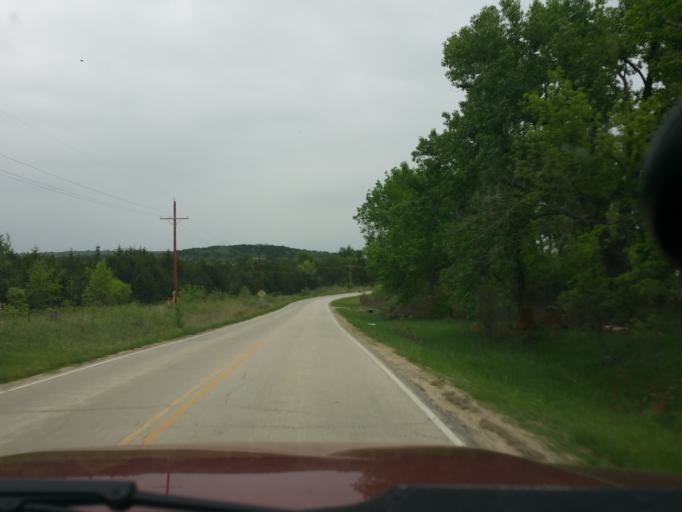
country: US
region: Kansas
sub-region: Riley County
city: Manhattan
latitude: 39.2650
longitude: -96.5719
